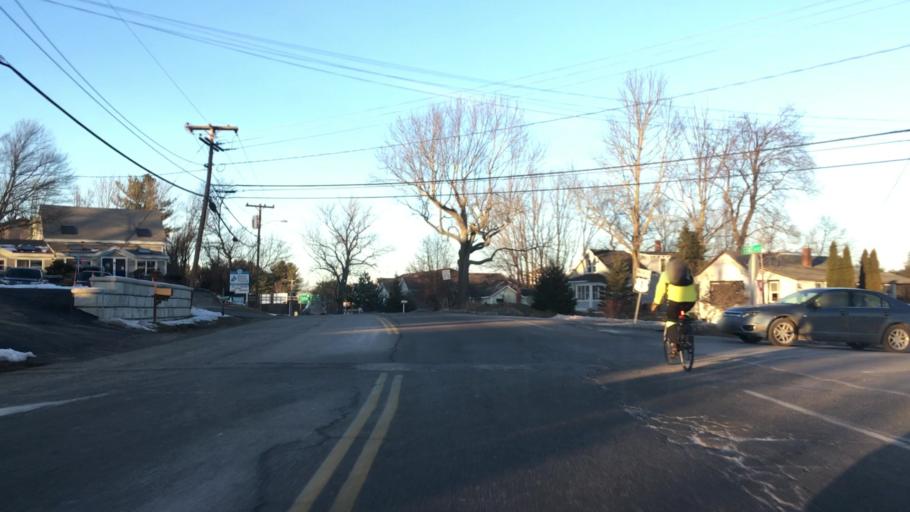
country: US
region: Maine
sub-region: York County
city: Kittery
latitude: 43.1017
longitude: -70.7434
